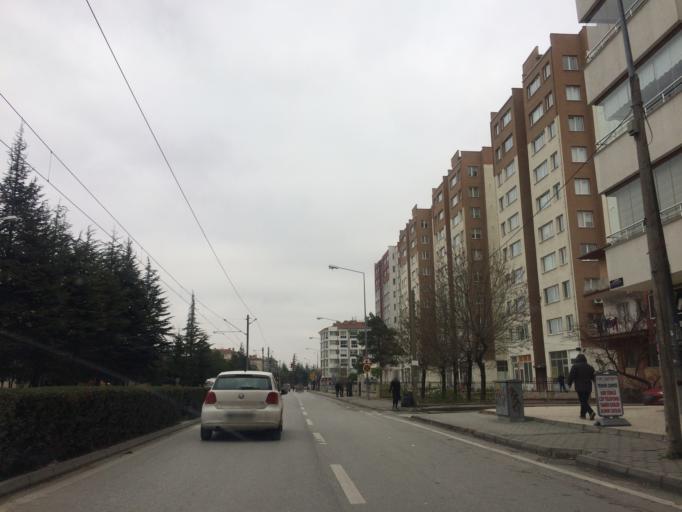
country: TR
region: Eskisehir
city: Eskisehir
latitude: 39.7898
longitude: 30.4875
